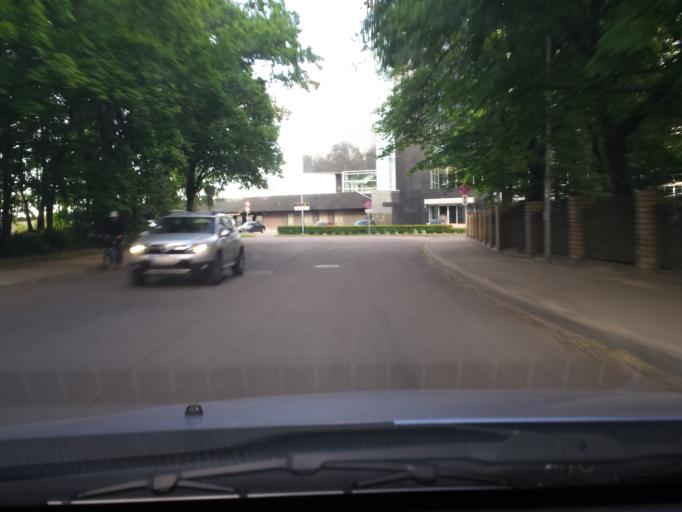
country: LV
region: Riga
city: Riga
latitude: 56.9483
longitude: 24.0881
